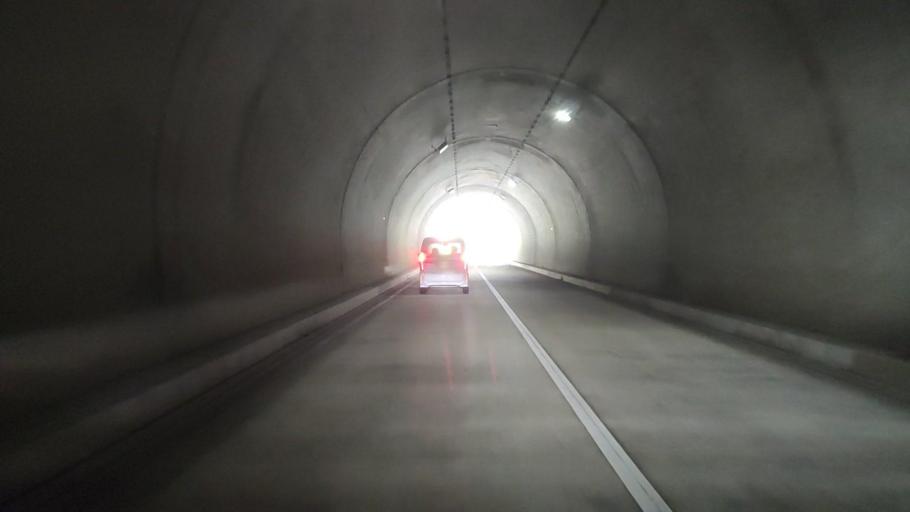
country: JP
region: Wakayama
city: Shingu
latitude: 33.8904
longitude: 135.8798
